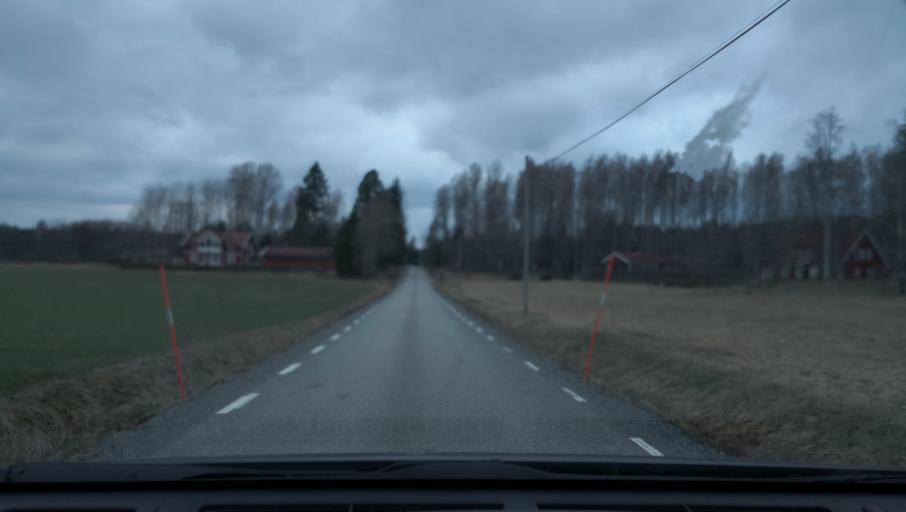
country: SE
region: Vaestmanland
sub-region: Kopings Kommun
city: Kolsva
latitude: 59.5626
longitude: 15.7384
